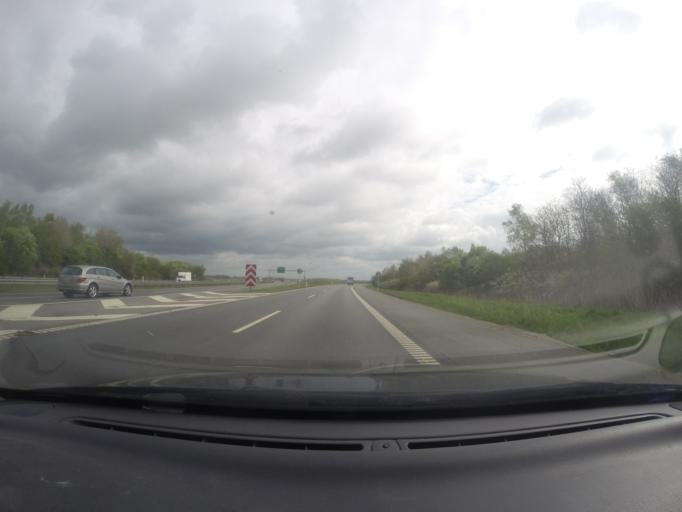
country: DK
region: Capital Region
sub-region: Ballerup Kommune
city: Ballerup
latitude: 55.6981
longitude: 12.3636
